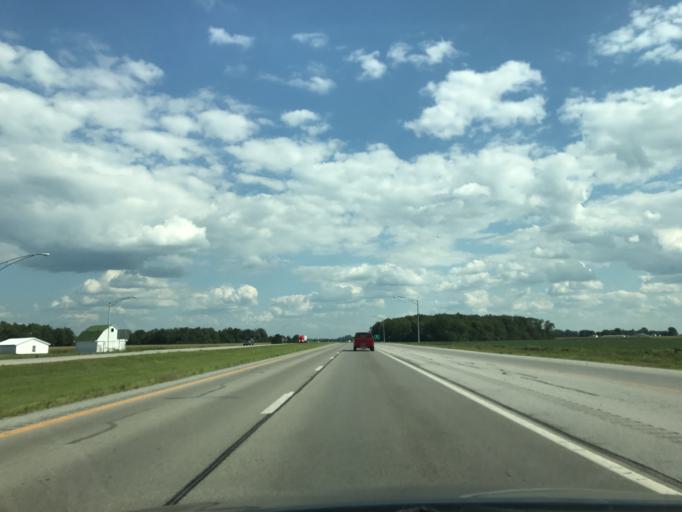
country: US
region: Ohio
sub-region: Allen County
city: Delphos
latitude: 40.8452
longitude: -84.3059
